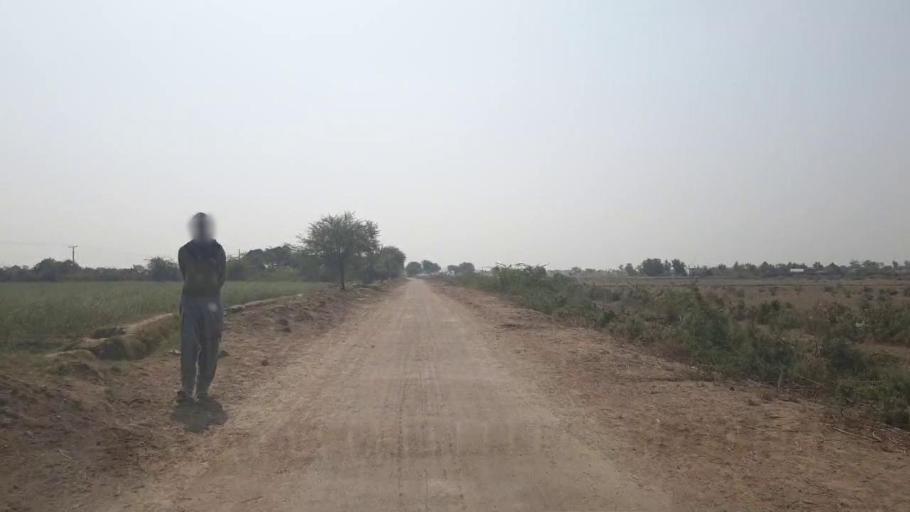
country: PK
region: Sindh
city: Dhoro Naro
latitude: 25.4398
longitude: 69.6262
